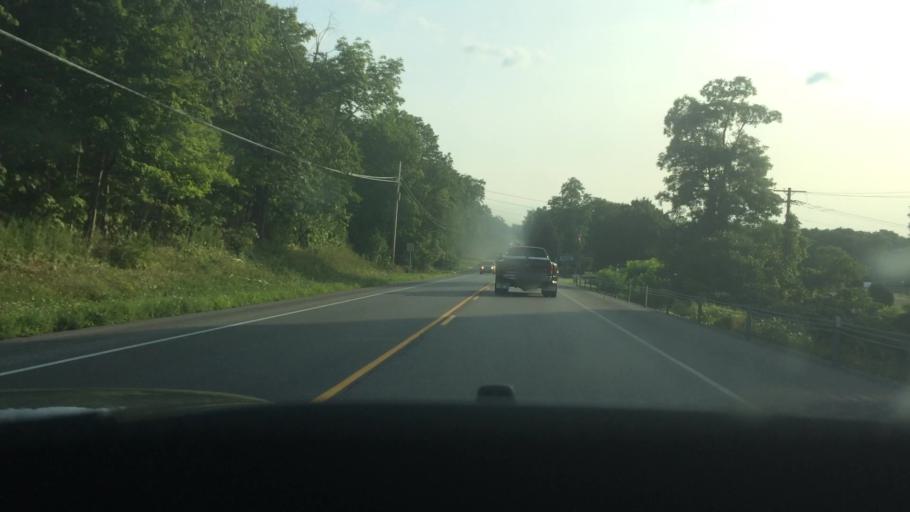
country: CA
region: Ontario
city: Prescott
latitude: 44.6747
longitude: -75.5263
